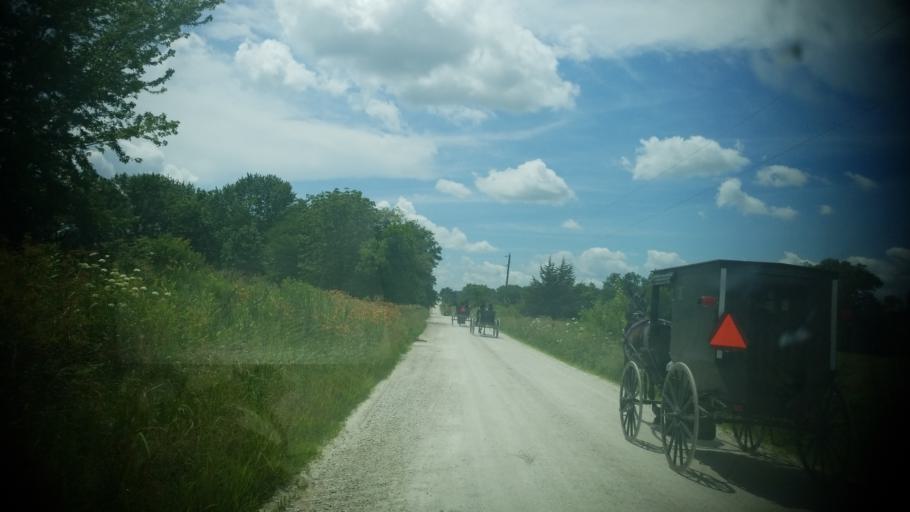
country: US
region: Missouri
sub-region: Pike County
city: Bowling Green
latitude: 39.3082
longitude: -91.2971
